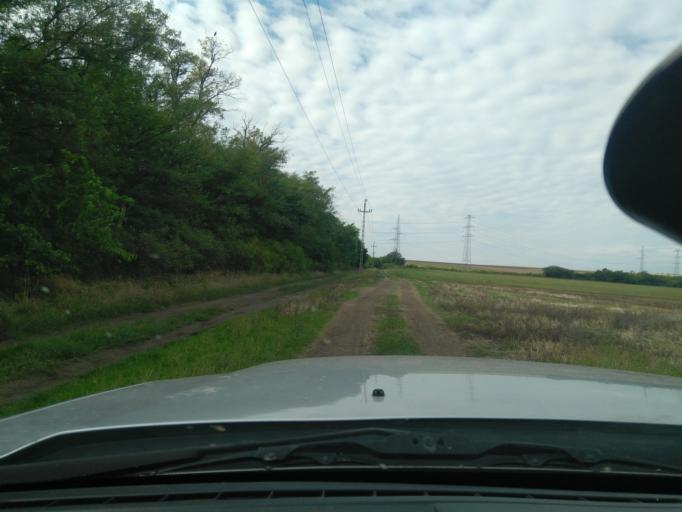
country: HU
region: Fejer
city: Val
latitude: 47.3698
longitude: 18.7129
